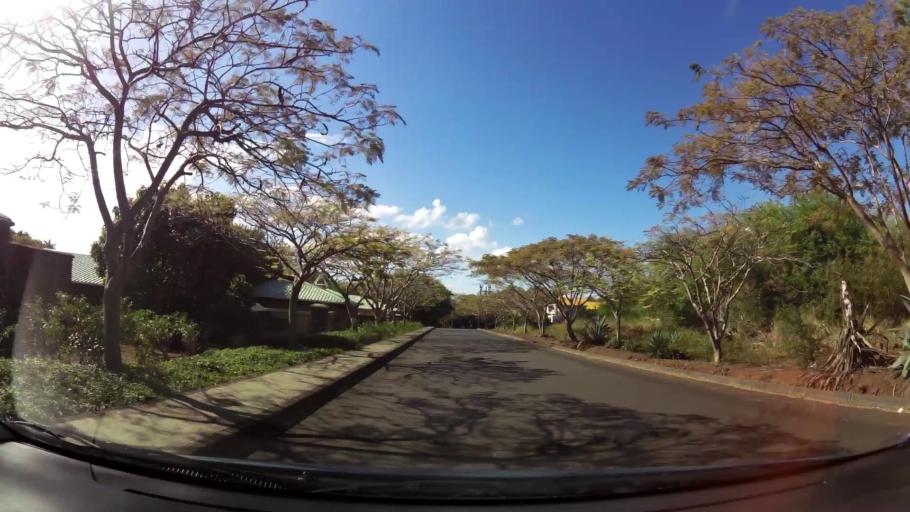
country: MU
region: Black River
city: Albion
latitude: -20.2189
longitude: 57.4005
